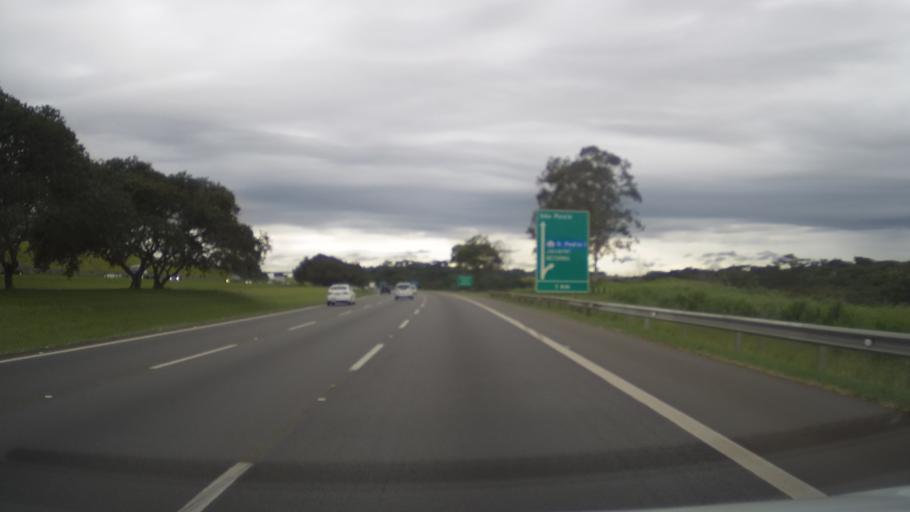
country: BR
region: Sao Paulo
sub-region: Campinas
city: Campinas
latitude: -23.0064
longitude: -47.0967
